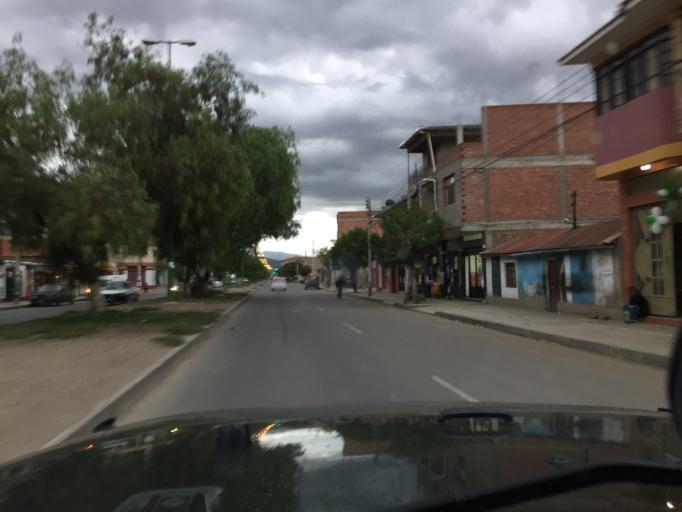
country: BO
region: Cochabamba
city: Cochabamba
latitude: -17.3971
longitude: -66.1967
